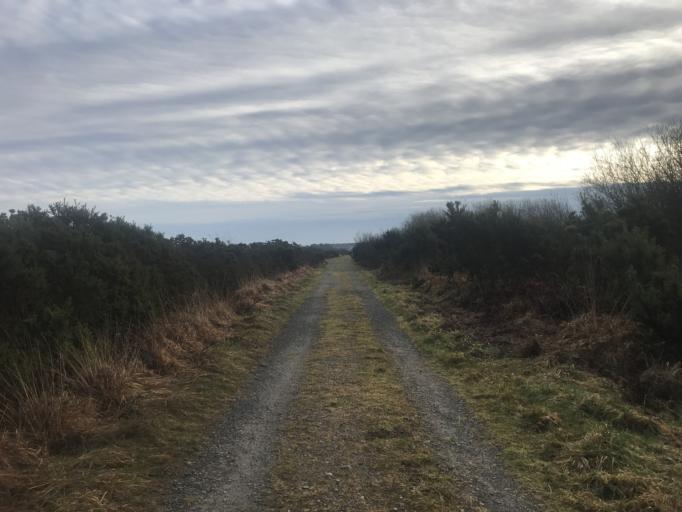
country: IE
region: Connaught
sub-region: County Galway
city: Gaillimh
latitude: 53.3218
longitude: -9.0126
